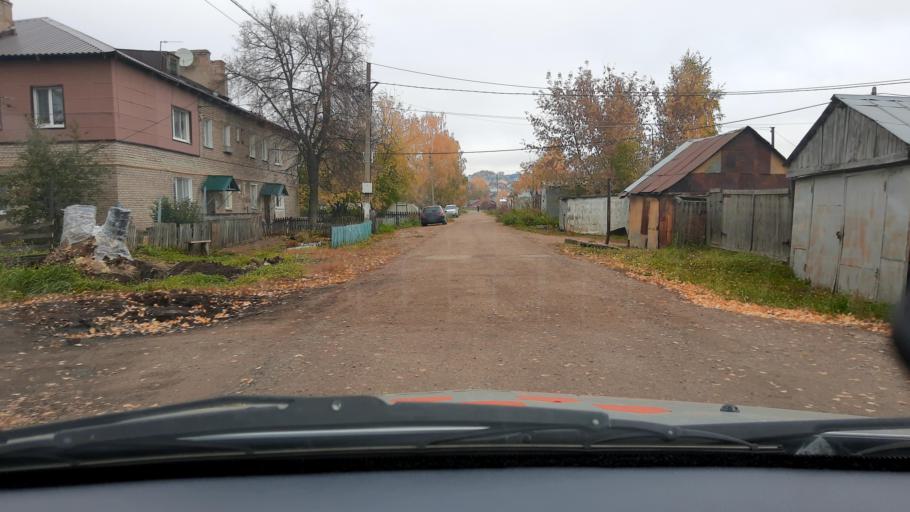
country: RU
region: Bashkortostan
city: Mikhaylovka
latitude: 54.8001
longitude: 55.8872
